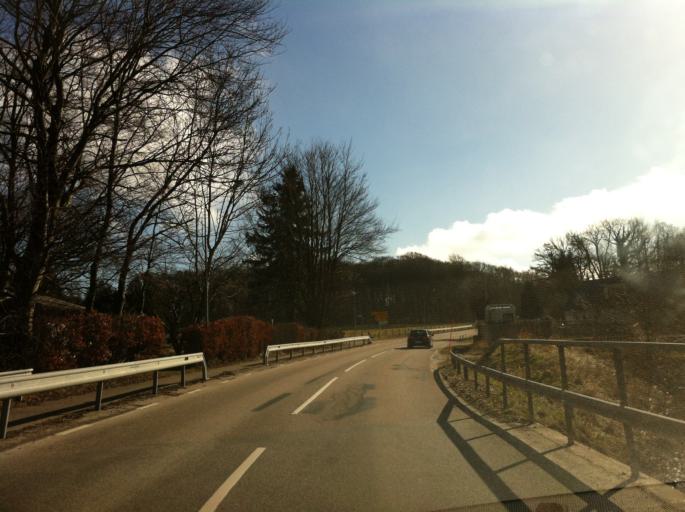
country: SE
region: Skane
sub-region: Bastads Kommun
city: Forslov
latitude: 56.3648
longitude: 12.8125
